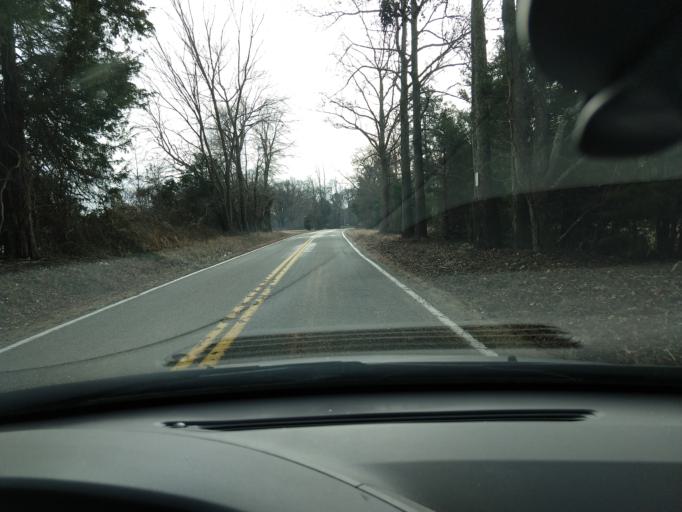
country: US
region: Virginia
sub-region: Henrico County
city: Fort Lee
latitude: 37.4385
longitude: -77.2350
